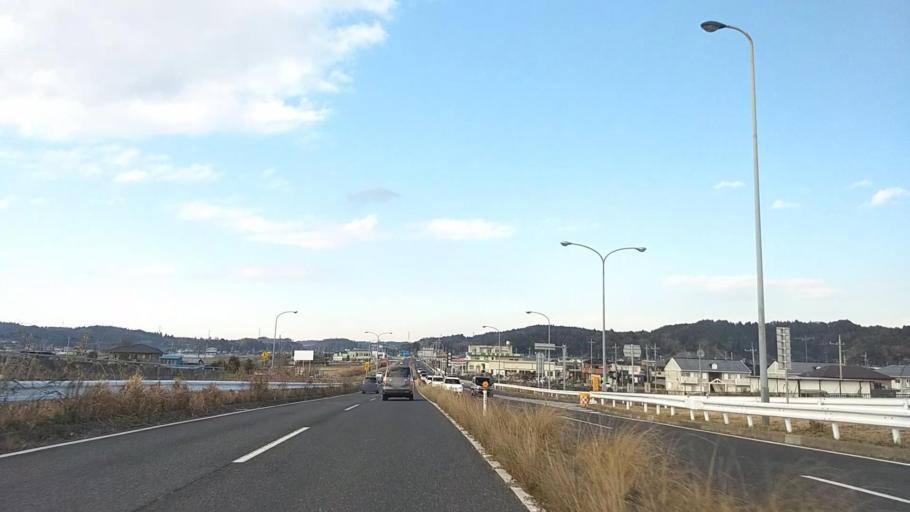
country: JP
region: Chiba
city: Togane
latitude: 35.5521
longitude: 140.3486
